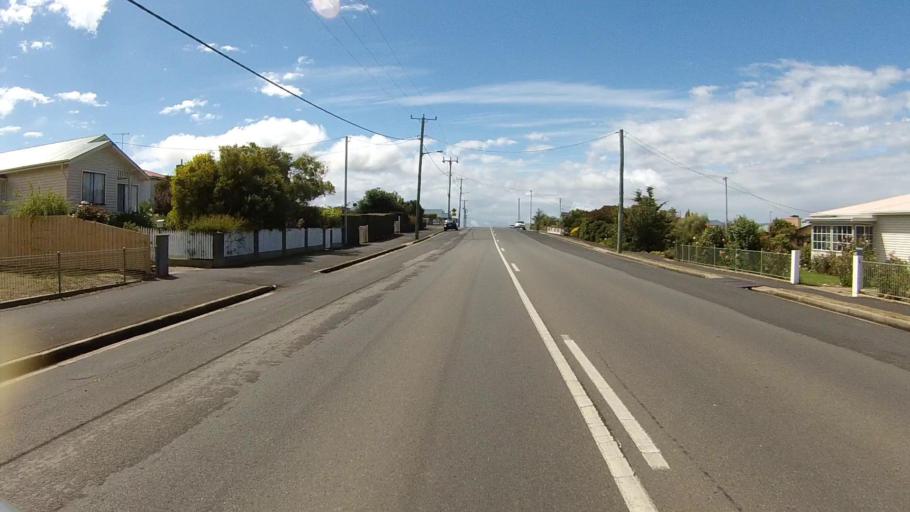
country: AU
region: Tasmania
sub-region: Break O'Day
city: St Helens
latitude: -42.1262
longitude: 148.0762
